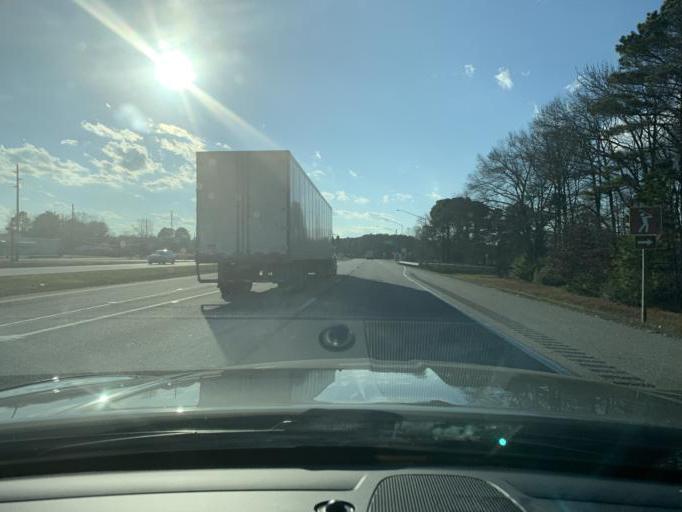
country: US
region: Maryland
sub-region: Queen Anne's County
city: Grasonville
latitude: 38.9854
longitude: -76.1599
